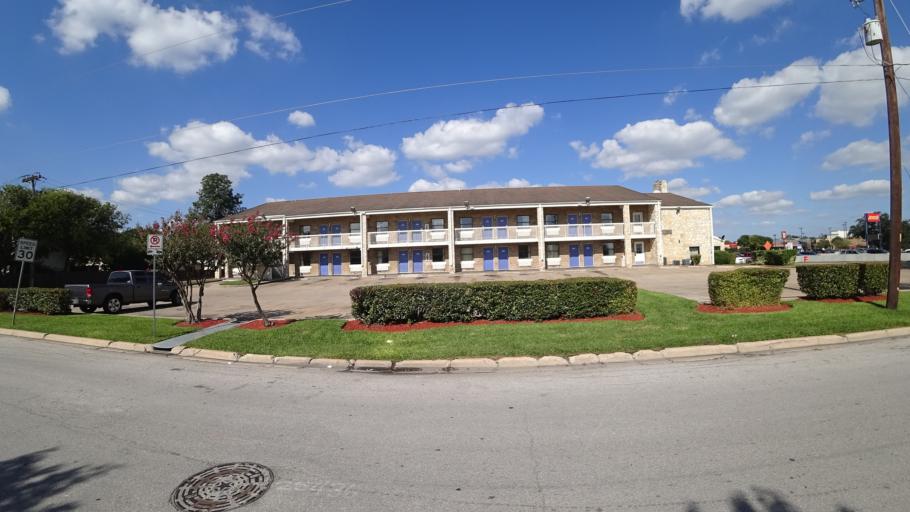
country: US
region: Texas
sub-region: Travis County
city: Austin
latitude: 30.3126
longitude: -97.7096
